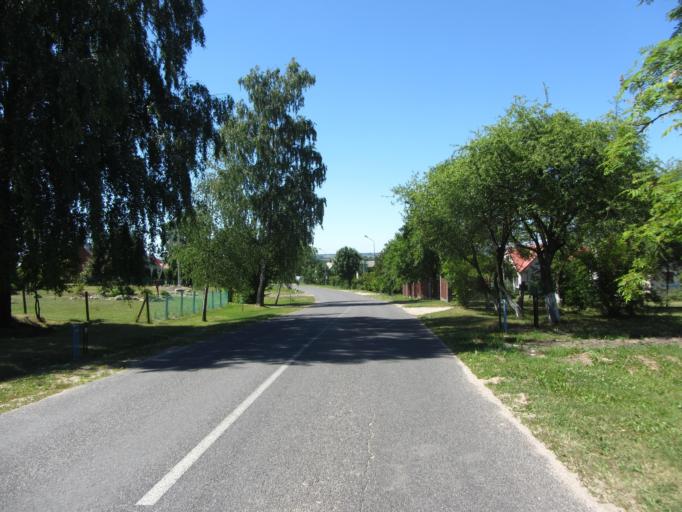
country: LT
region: Vilnius County
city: Elektrenai
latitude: 54.7941
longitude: 24.7136
